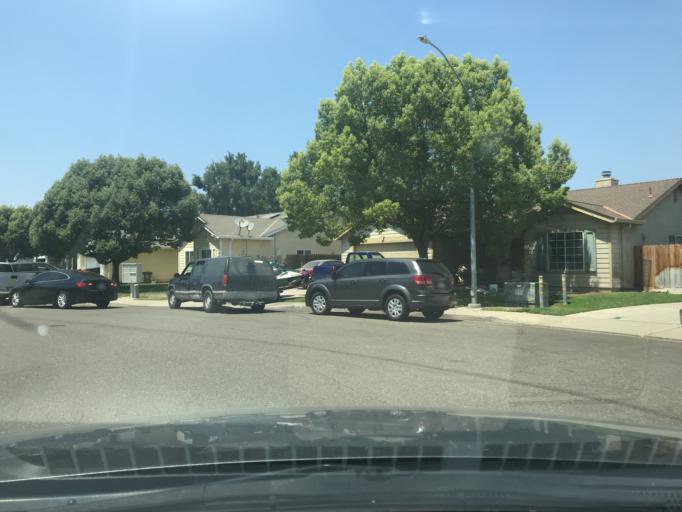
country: US
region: California
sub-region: Merced County
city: Atwater
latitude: 37.3523
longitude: -120.5799
